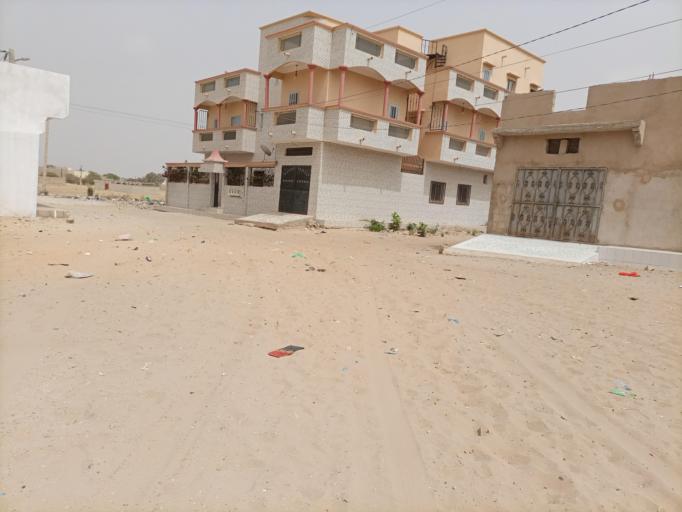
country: SN
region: Saint-Louis
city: Saint-Louis
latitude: 16.0381
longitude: -16.4402
